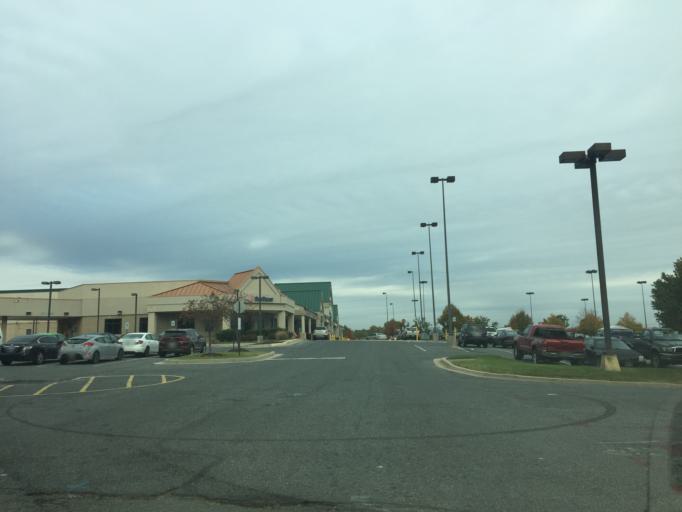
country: US
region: Maryland
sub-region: Baltimore County
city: Dundalk
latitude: 39.2767
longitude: -76.5053
